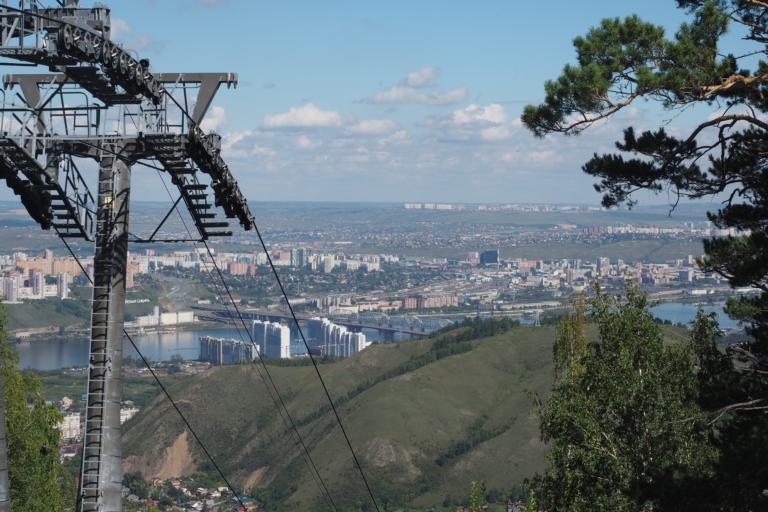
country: RU
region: Krasnoyarskiy
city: Krasnoyarsk
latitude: 55.9491
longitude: 92.7865
